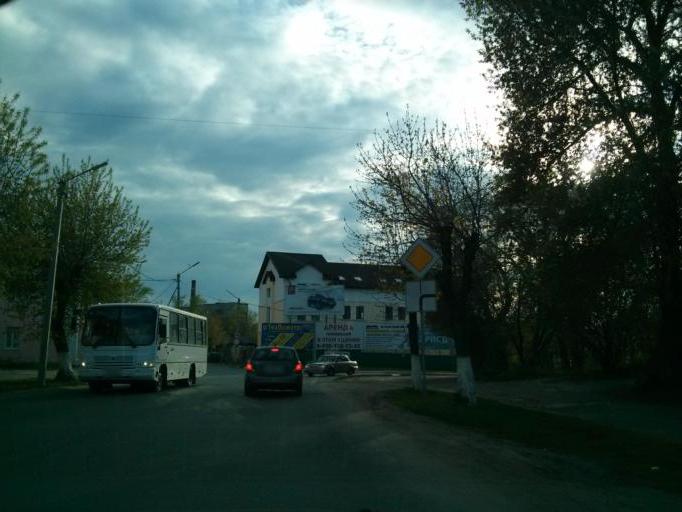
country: RU
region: Vladimir
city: Murom
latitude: 55.5781
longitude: 42.0415
